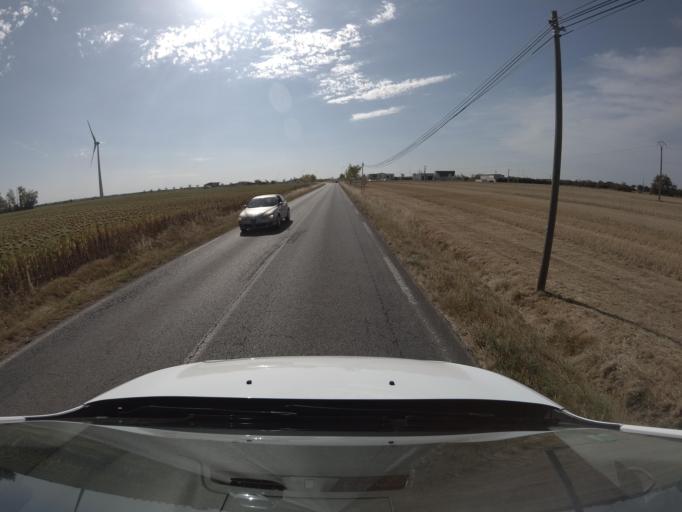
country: FR
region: Poitou-Charentes
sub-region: Departement des Deux-Sevres
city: Mauze-Thouarsais
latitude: 46.9987
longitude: -0.2817
